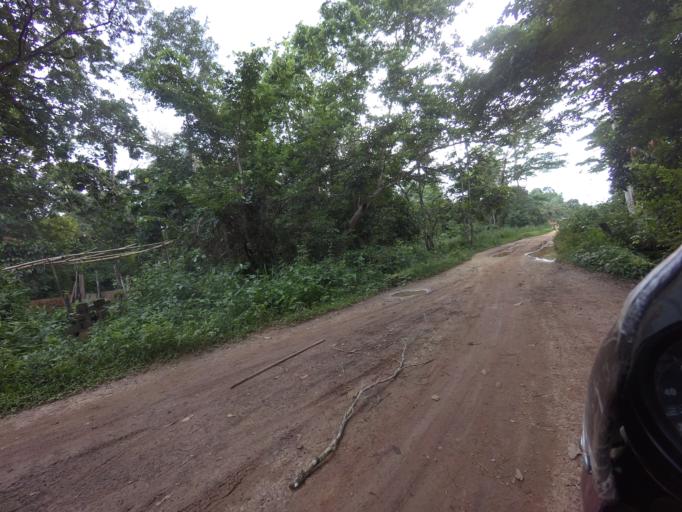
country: SL
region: Eastern Province
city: Jojoima
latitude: 7.8091
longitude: -10.8143
